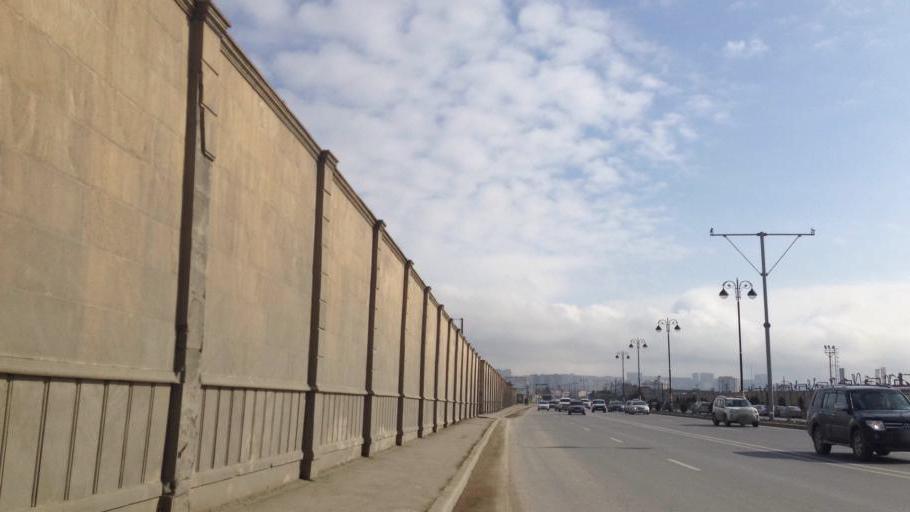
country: AZ
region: Baki
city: Baku
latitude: 40.3769
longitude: 49.9107
